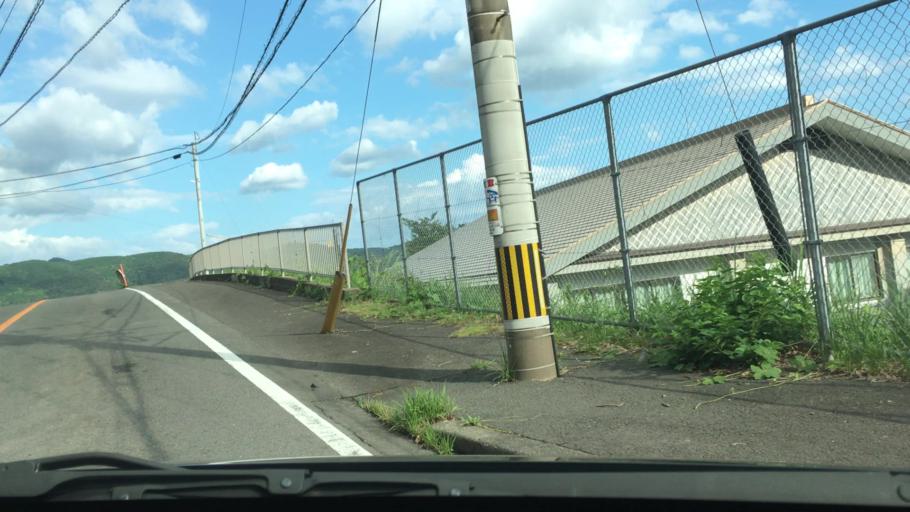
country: JP
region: Nagasaki
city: Togitsu
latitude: 32.8242
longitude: 129.7571
